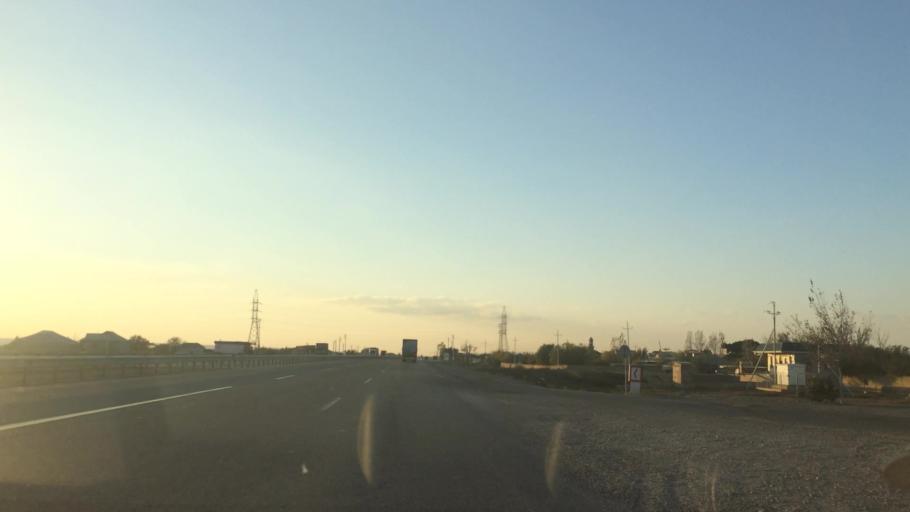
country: AZ
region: Baki
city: Qobustan
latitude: 39.9686
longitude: 49.2700
